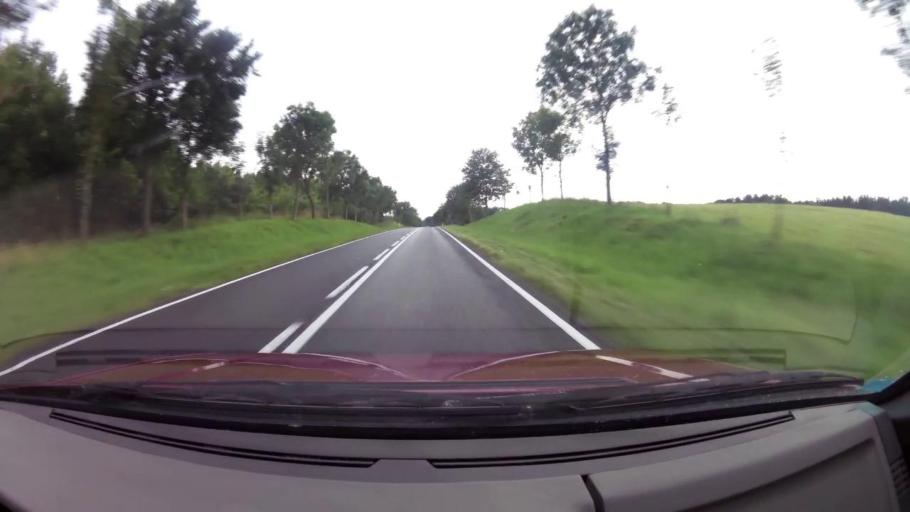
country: PL
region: West Pomeranian Voivodeship
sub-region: Powiat lobeski
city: Wegorzyno
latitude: 53.5255
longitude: 15.5181
